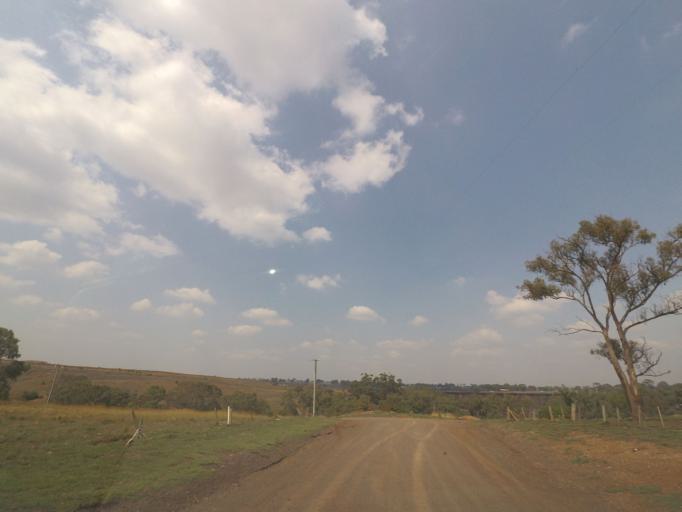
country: AU
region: Victoria
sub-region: Melton
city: Brookfield
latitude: -37.7133
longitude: 144.5442
